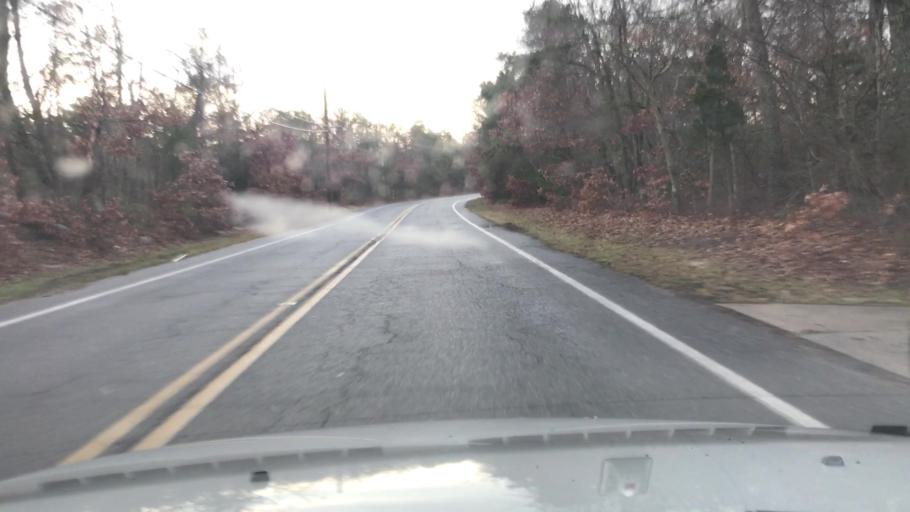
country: US
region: New Jersey
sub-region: Cape May County
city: Sea Isle City
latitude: 39.1924
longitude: -74.7568
